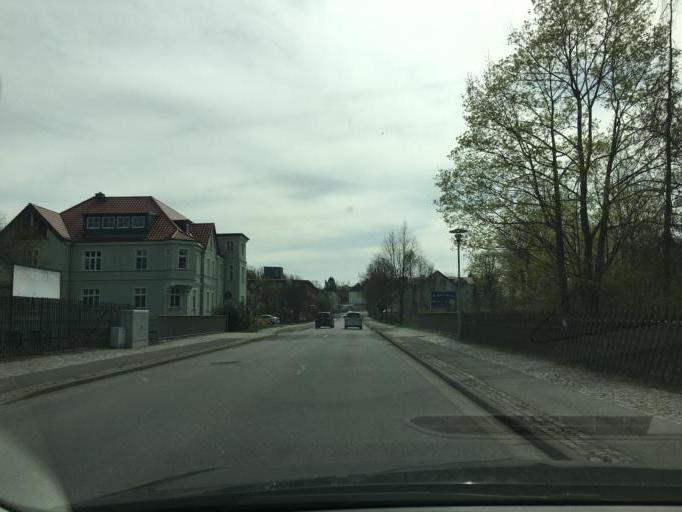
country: DE
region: Brandenburg
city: Spremberg
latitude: 51.5698
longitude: 14.3837
